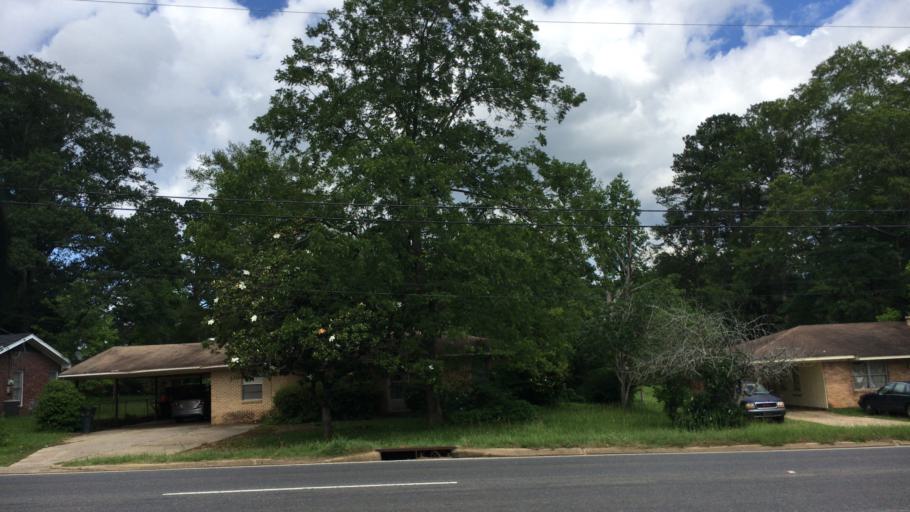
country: US
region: Louisiana
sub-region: Lincoln Parish
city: Ruston
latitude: 32.5143
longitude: -92.6385
